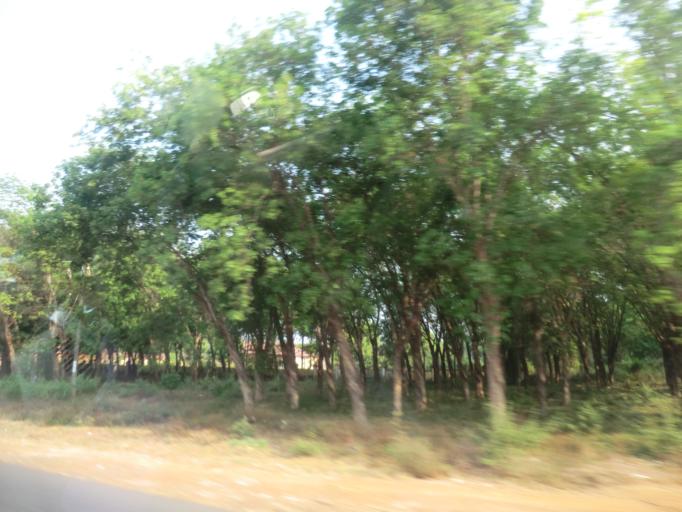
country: VN
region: Dong Nai
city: Thong Nhat
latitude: 10.9425
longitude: 107.1483
